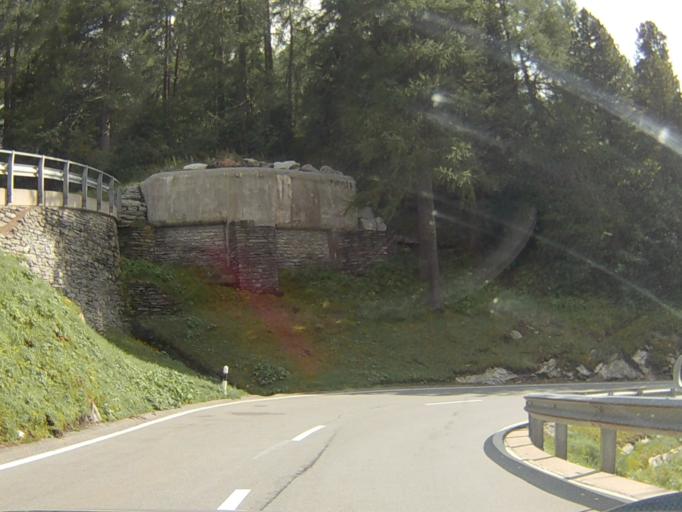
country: CH
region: Grisons
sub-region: Maloja District
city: Silvaplana
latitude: 46.3960
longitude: 9.6933
